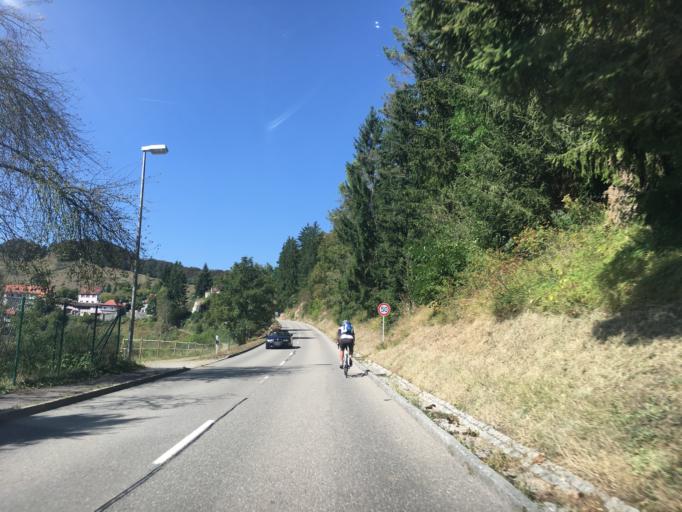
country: DE
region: Baden-Wuerttemberg
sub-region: Tuebingen Region
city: Hayingen
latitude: 48.3214
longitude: 9.5055
